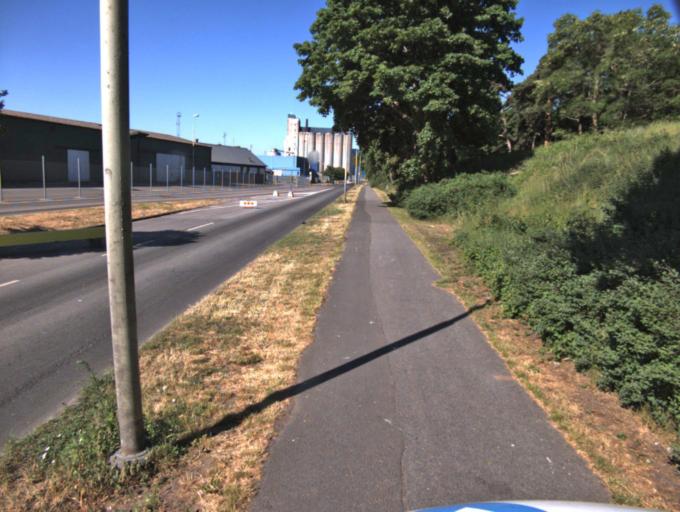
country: SE
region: Skane
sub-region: Kristianstads Kommun
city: Ahus
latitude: 55.9286
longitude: 14.3121
